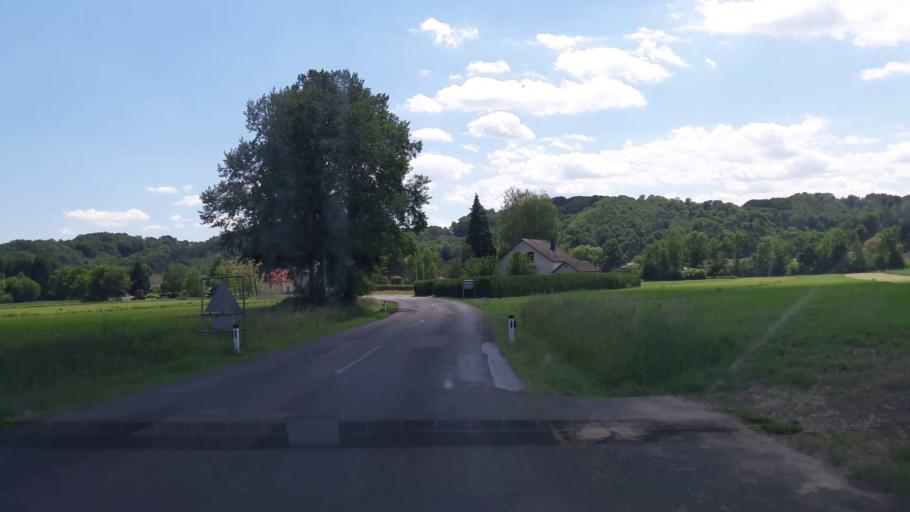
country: AT
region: Burgenland
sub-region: Politischer Bezirk Jennersdorf
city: Jennersdorf
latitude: 46.9553
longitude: 16.1181
